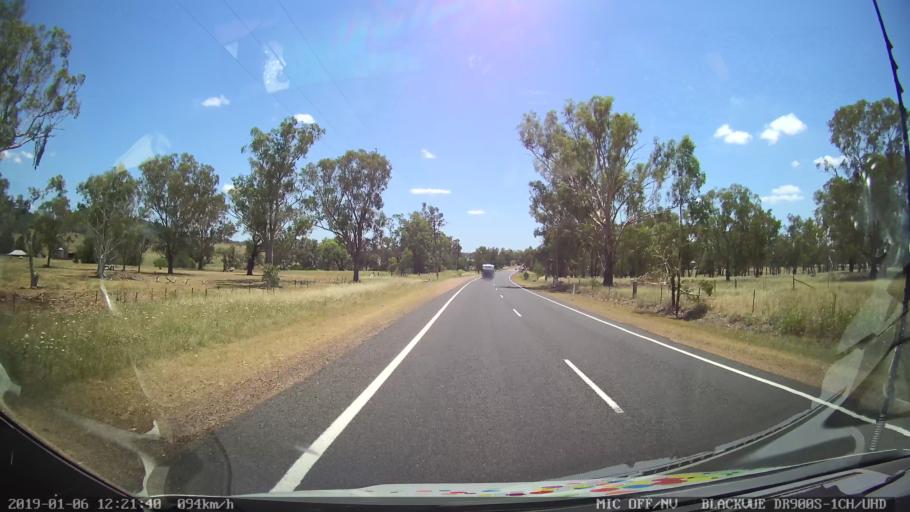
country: AU
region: New South Wales
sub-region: Tamworth Municipality
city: Phillip
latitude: -31.2714
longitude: 150.7838
